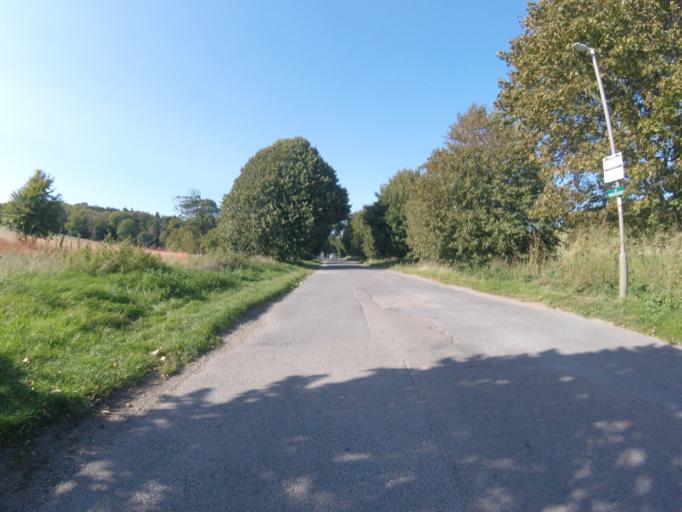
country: GB
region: England
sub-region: Brighton and Hove
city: Brighton
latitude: 50.8635
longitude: -0.0946
